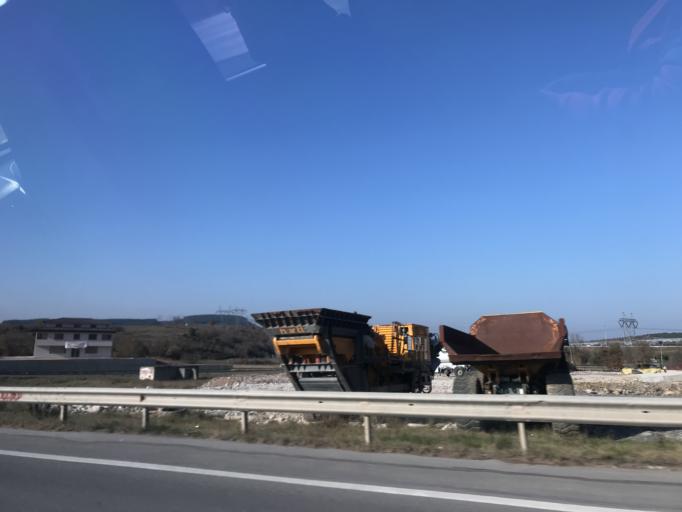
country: TR
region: Istanbul
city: Sultanbeyli
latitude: 40.9349
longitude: 29.3580
